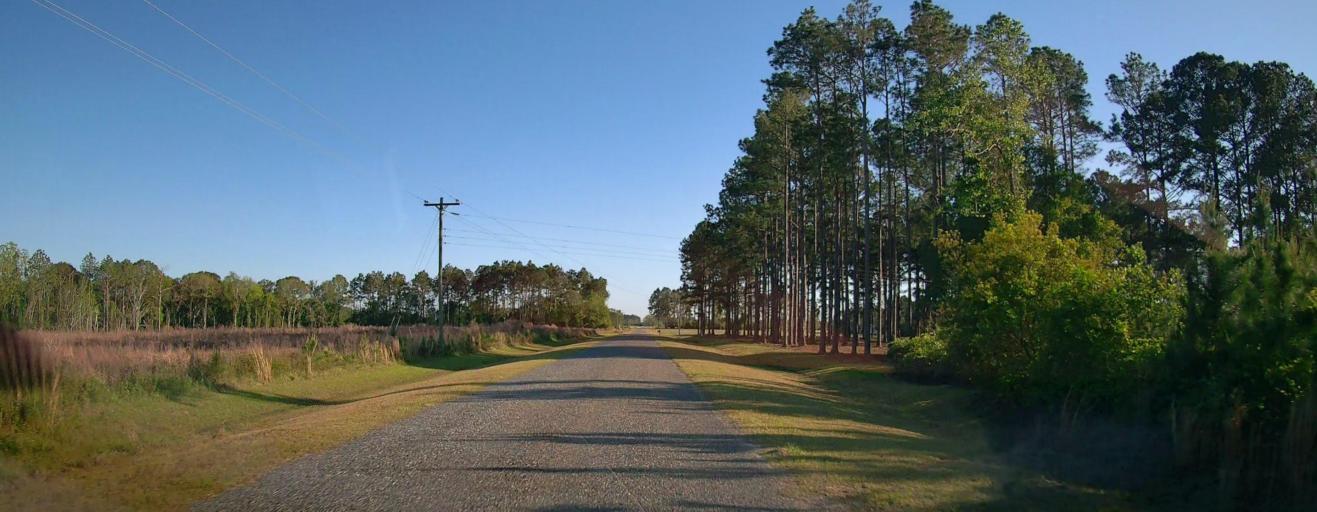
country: US
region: Georgia
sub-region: Ben Hill County
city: Fitzgerald
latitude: 31.6737
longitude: -83.1467
